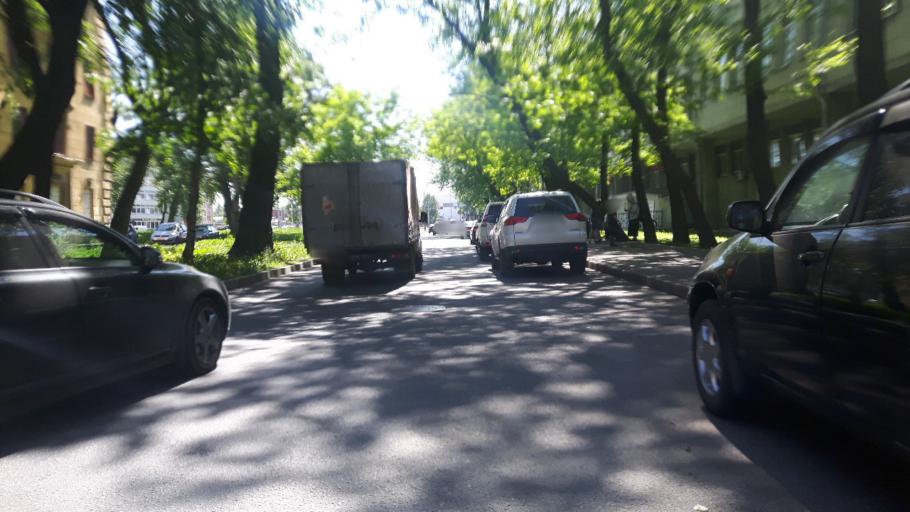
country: RU
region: St.-Petersburg
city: Admiralteisky
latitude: 59.8995
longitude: 30.2869
